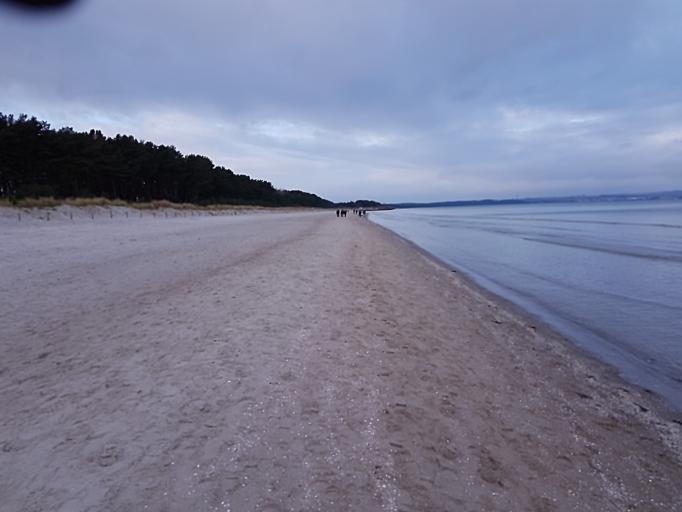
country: DE
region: Mecklenburg-Vorpommern
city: Ostseebad Binz
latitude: 54.4325
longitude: 13.5825
